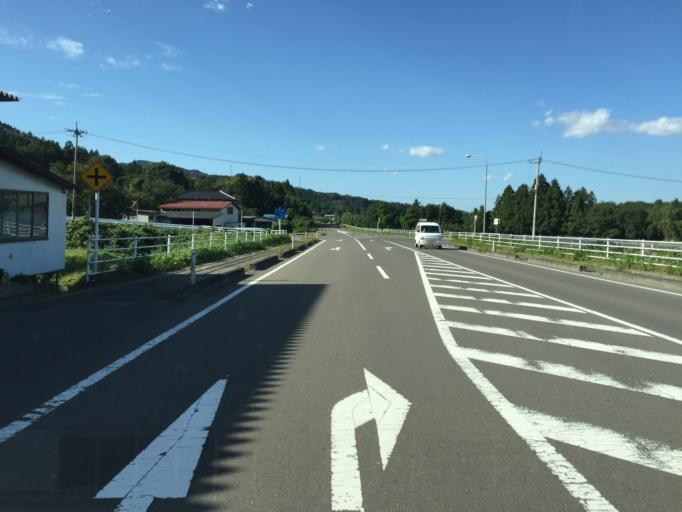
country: JP
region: Miyagi
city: Marumori
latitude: 37.8868
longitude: 140.7742
